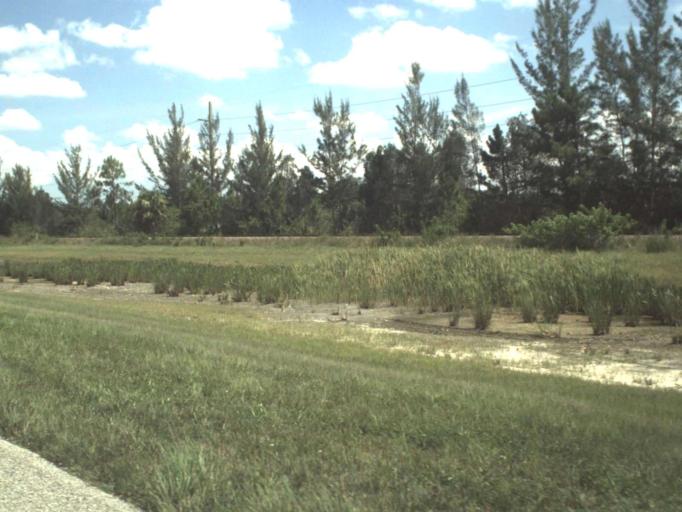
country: US
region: Florida
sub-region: Palm Beach County
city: Limestone Creek
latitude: 26.8884
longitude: -80.2700
